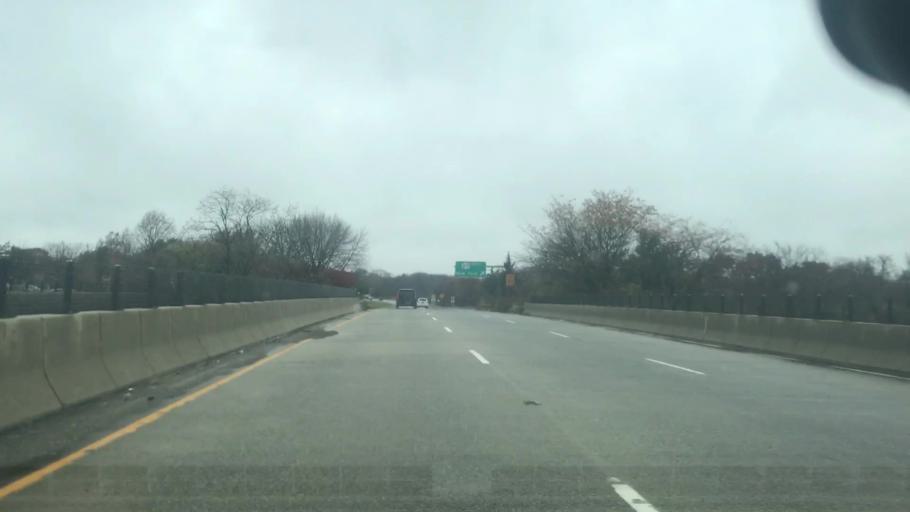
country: US
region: New York
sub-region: Suffolk County
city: North Babylon
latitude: 40.7179
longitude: -73.3141
